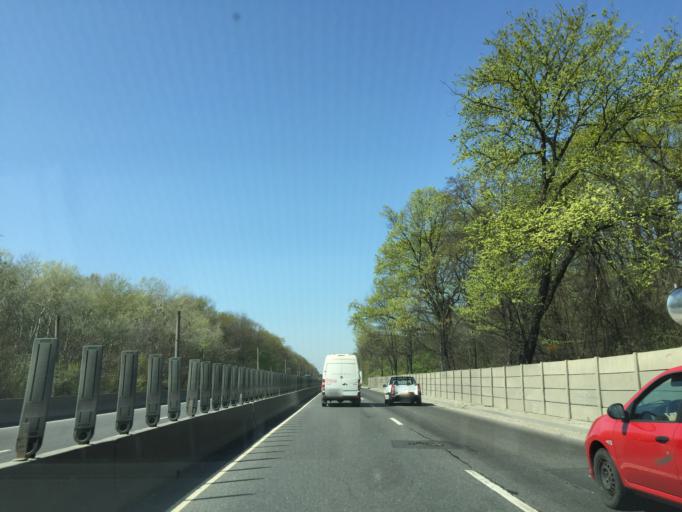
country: RO
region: Ilfov
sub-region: Comuna Tunari
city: Tunari
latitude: 44.5393
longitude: 26.1182
